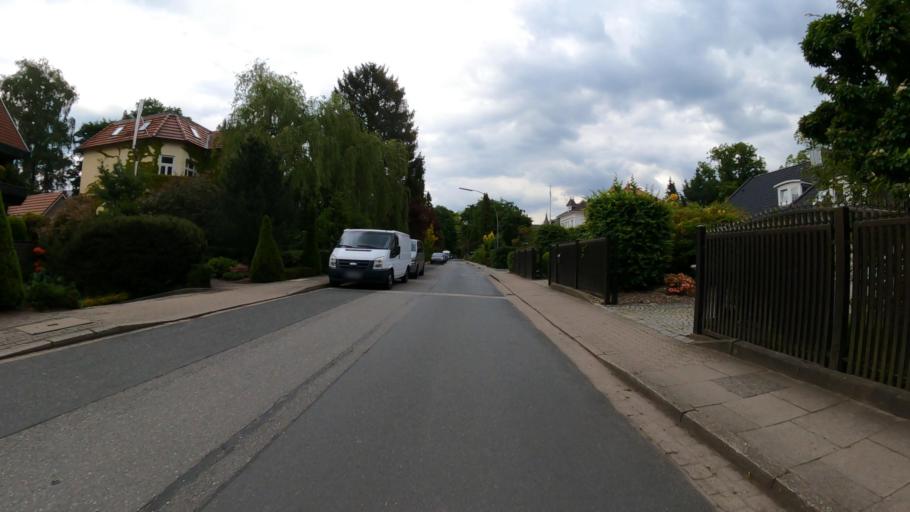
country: DE
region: Schleswig-Holstein
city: Rellingen
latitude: 53.6548
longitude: 9.8139
